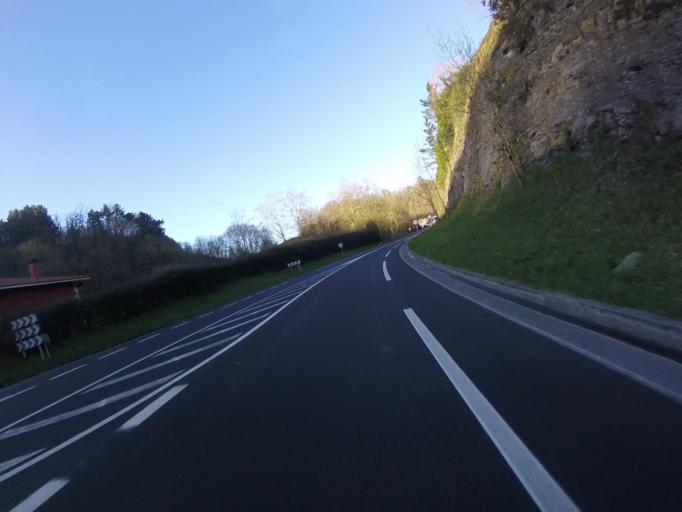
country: ES
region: Basque Country
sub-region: Provincia de Guipuzcoa
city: Errenteria
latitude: 43.2909
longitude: -1.8842
